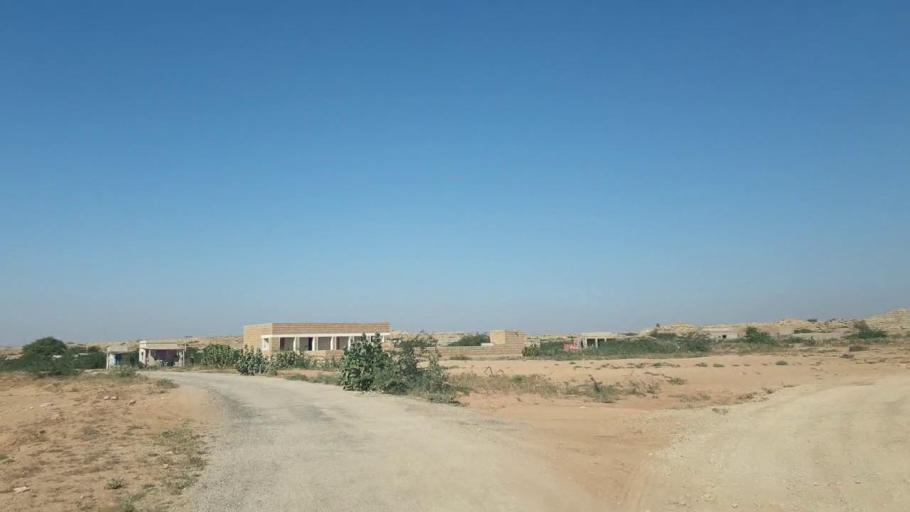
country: PK
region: Sindh
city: Gharo
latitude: 25.0888
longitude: 67.5368
